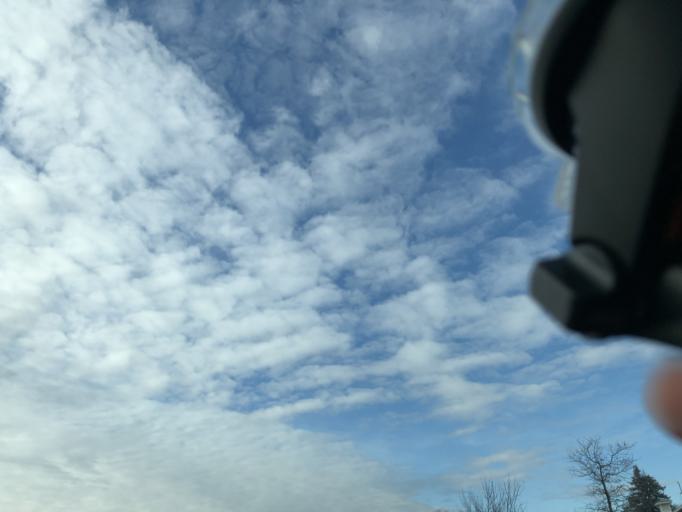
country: US
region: Michigan
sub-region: Wayne County
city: Taylor
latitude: 42.2125
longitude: -83.2524
